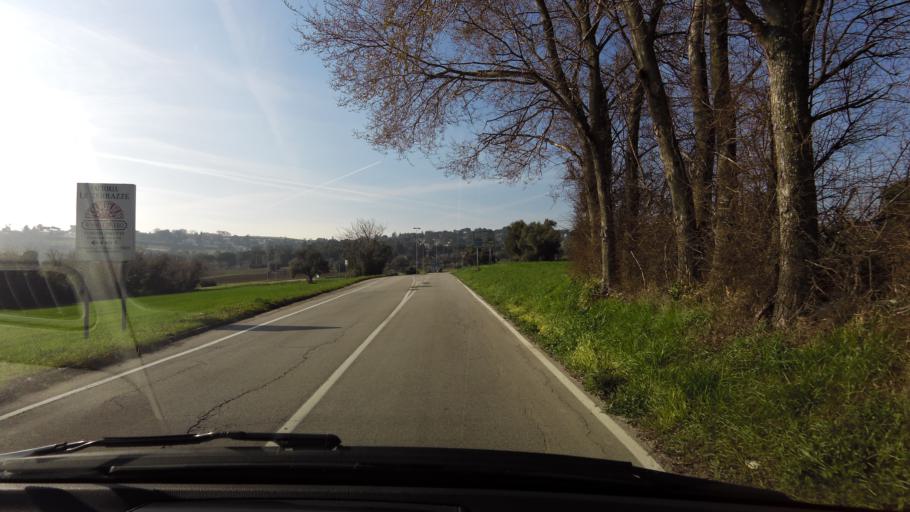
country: IT
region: The Marches
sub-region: Provincia di Ancona
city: Marcelli
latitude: 43.4990
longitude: 13.6185
